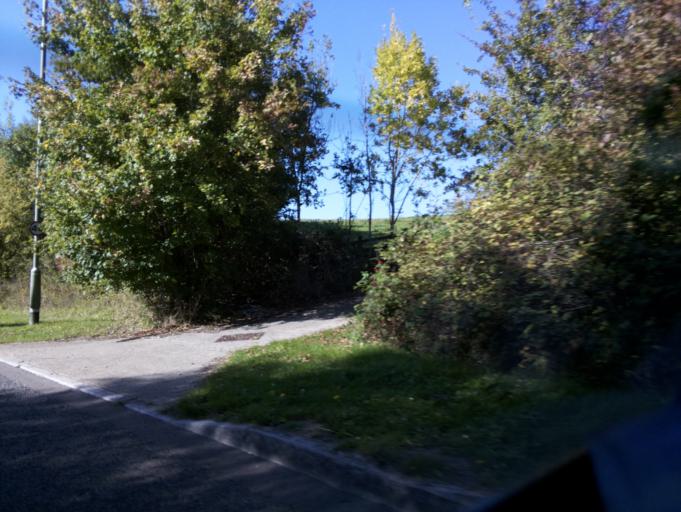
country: GB
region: England
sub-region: West Berkshire
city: Thatcham
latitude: 51.4125
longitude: -1.2536
